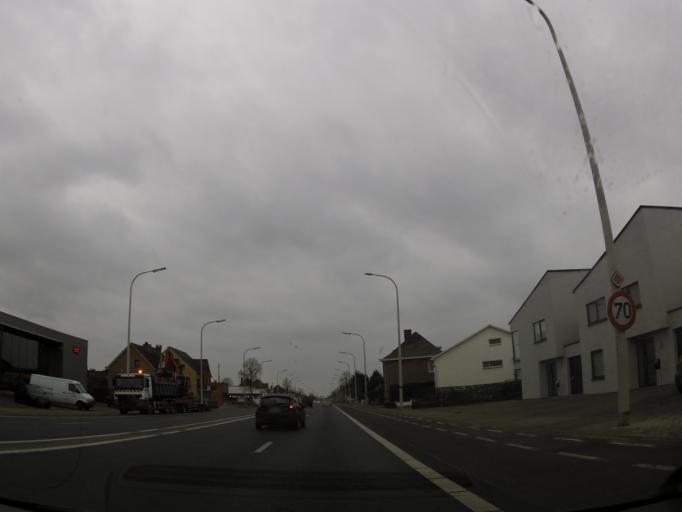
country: NL
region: Limburg
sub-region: Gemeente Stein
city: Berg
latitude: 51.0170
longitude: 5.7258
